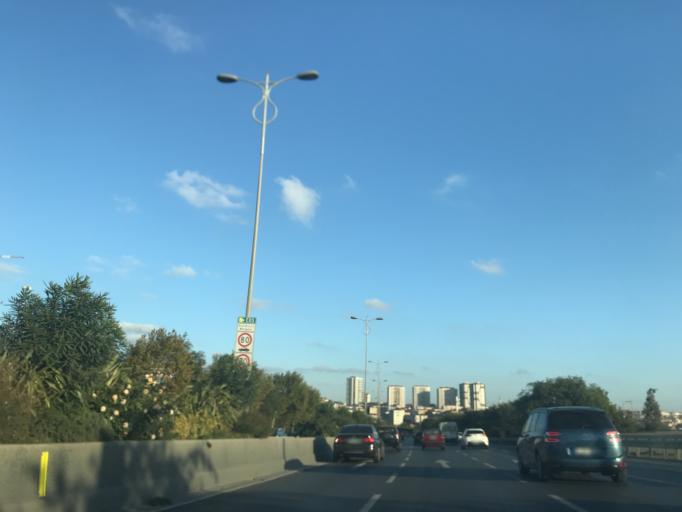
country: TR
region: Istanbul
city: Mahmutbey
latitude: 41.0583
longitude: 28.8456
